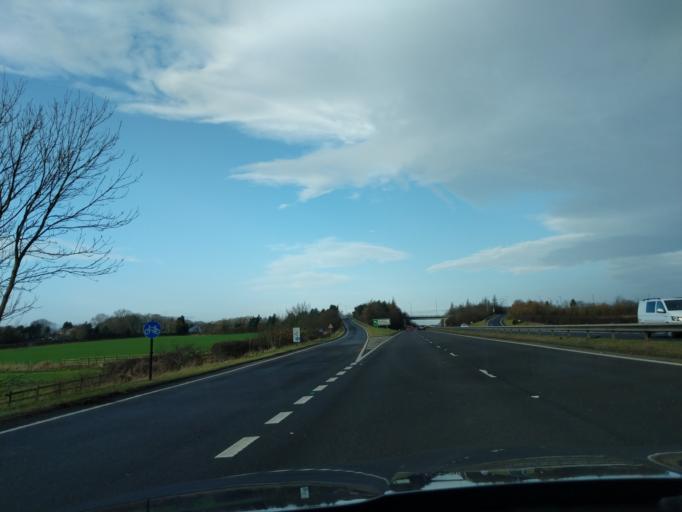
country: GB
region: England
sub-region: Newcastle upon Tyne
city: Dinnington
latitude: 55.0251
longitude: -1.7040
